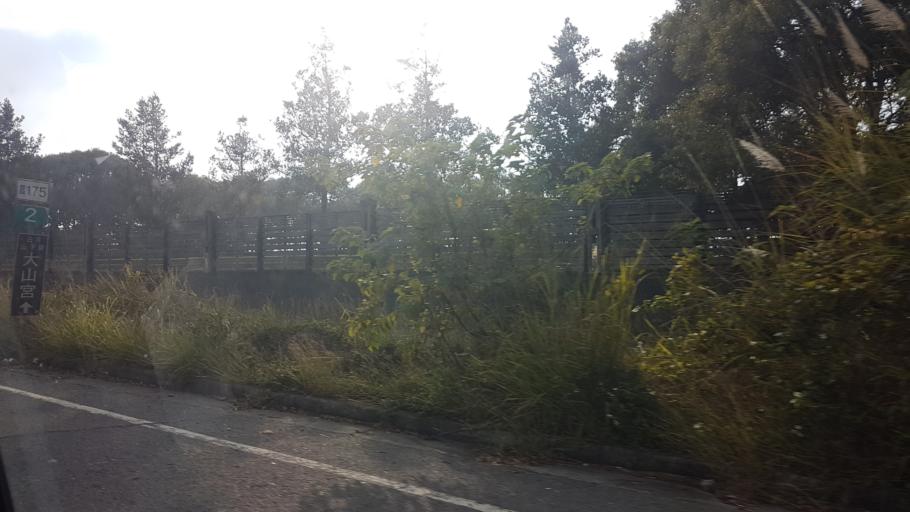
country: TW
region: Taiwan
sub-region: Chiayi
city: Jiayi Shi
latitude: 23.4242
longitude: 120.4318
